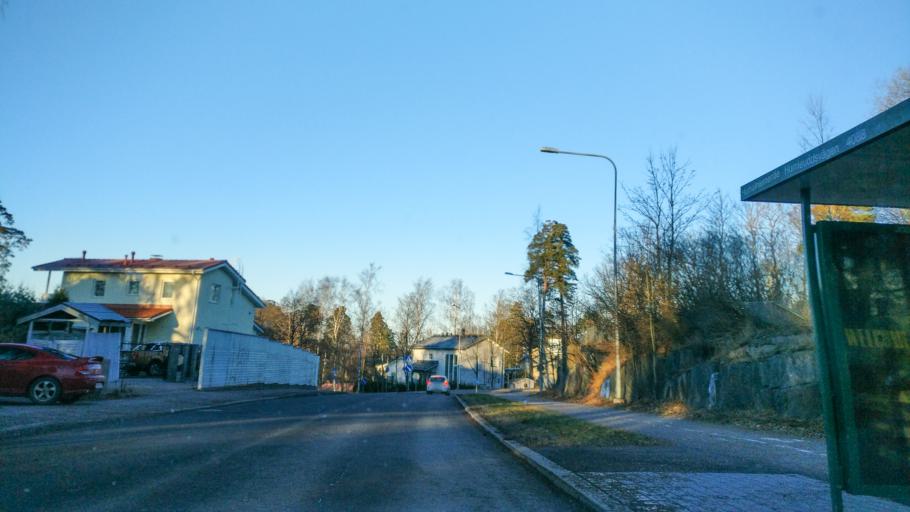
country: FI
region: Uusimaa
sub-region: Helsinki
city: Vantaa
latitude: 60.1829
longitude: 25.0505
